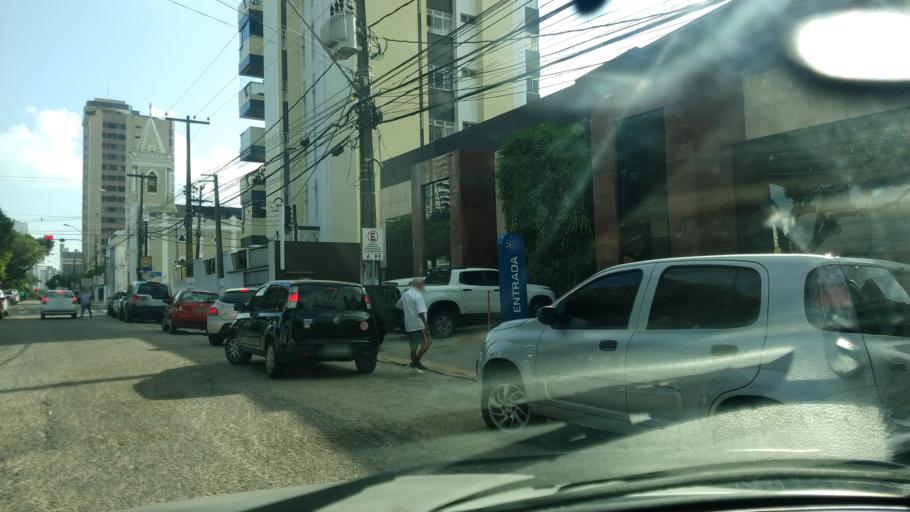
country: BR
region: Rio Grande do Norte
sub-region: Natal
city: Natal
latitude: -5.7924
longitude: -35.2002
